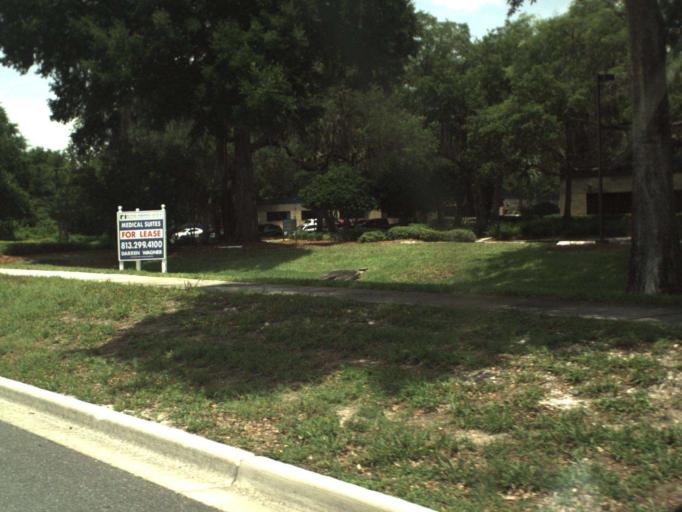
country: US
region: Florida
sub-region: Seminole County
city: Oviedo
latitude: 28.6636
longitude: -81.2244
